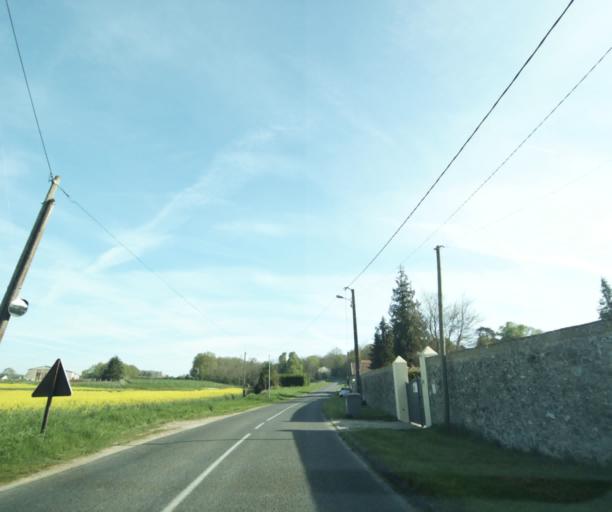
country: FR
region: Ile-de-France
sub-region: Departement de Seine-et-Marne
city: Vernou-la-Celle-sur-Seine
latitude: 48.4566
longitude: 2.8600
